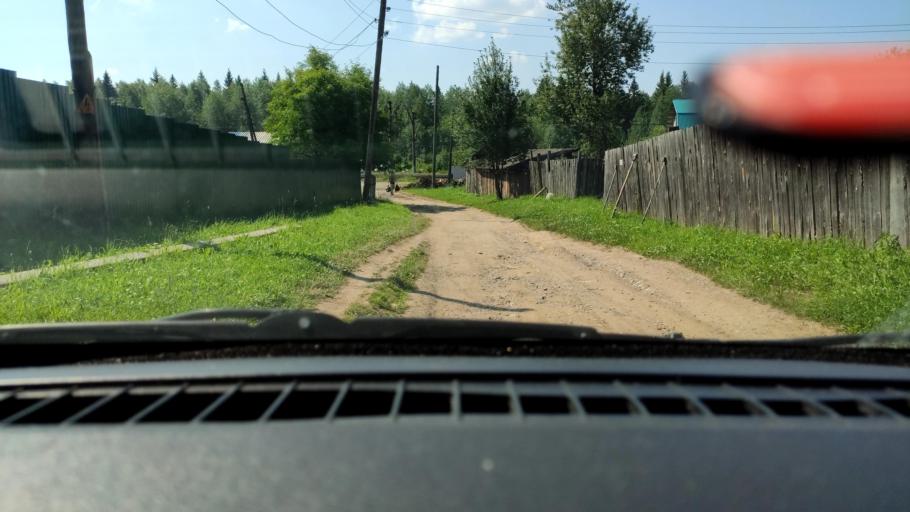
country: RU
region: Perm
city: Overyata
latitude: 58.1206
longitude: 55.8154
